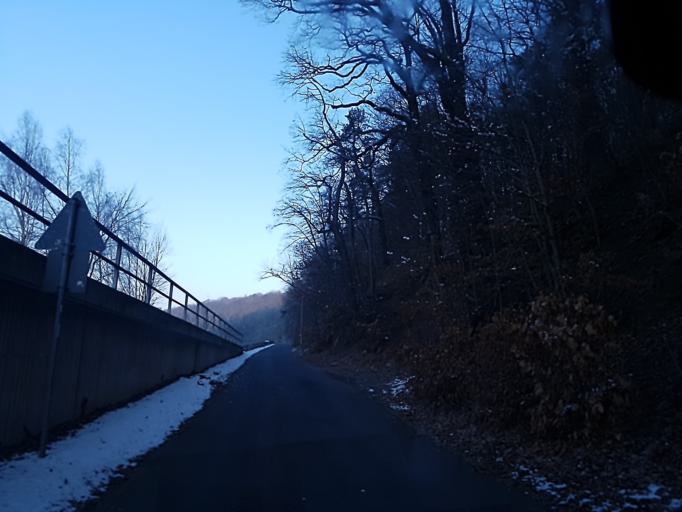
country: DE
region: Saxony
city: Grossweitzschen
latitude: 51.1538
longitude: 13.0113
